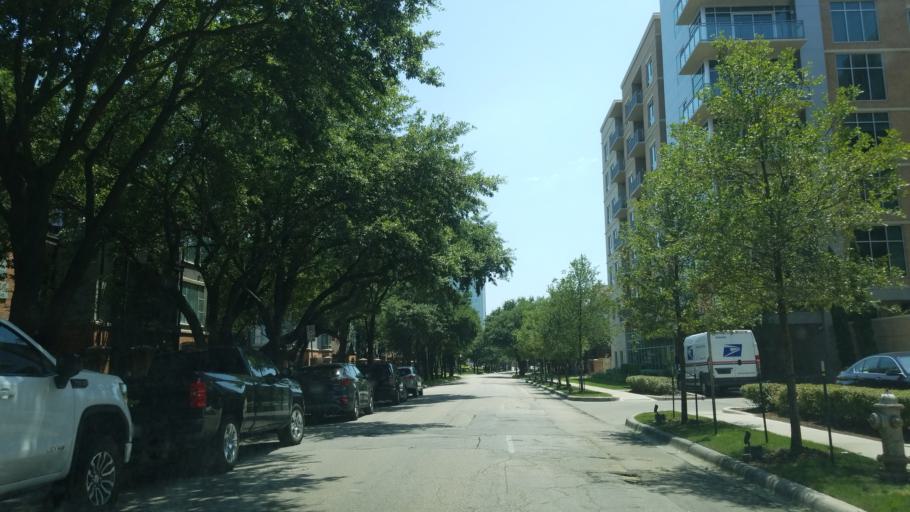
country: US
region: Texas
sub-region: Dallas County
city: Highland Park
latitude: 32.8262
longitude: -96.7872
